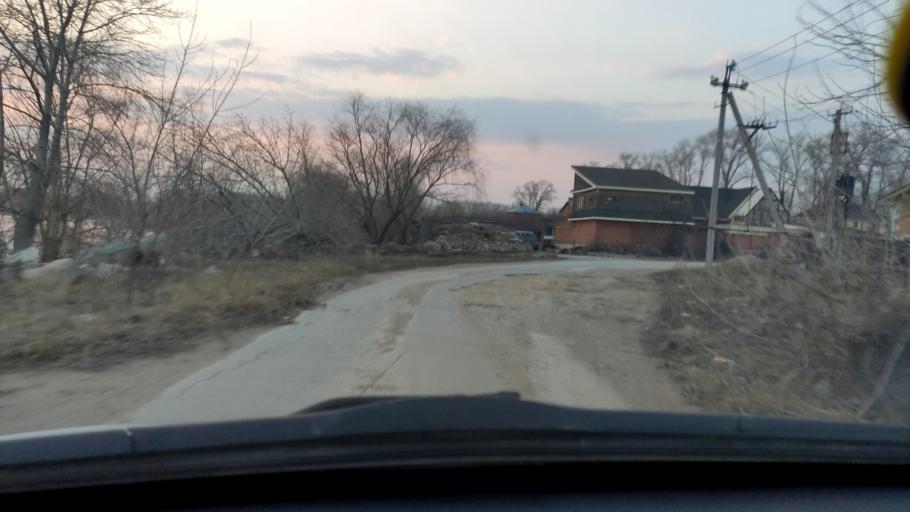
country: RU
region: Samara
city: Zhigulevsk
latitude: 53.4555
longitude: 49.5174
